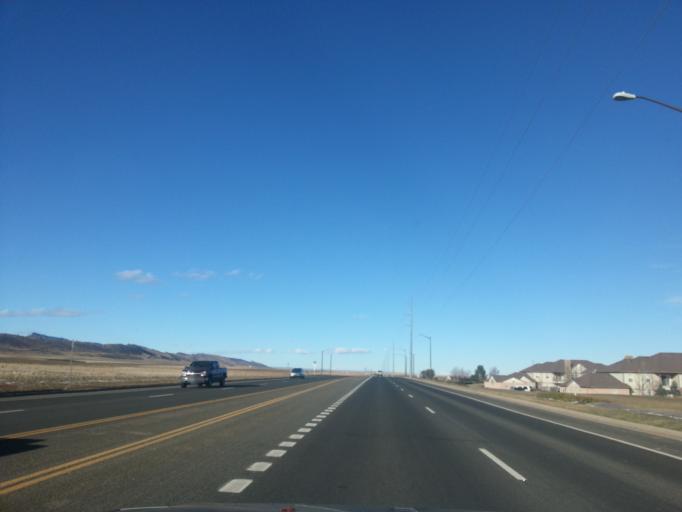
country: US
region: Colorado
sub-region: Larimer County
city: Loveland
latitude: 40.4416
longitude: -105.1155
